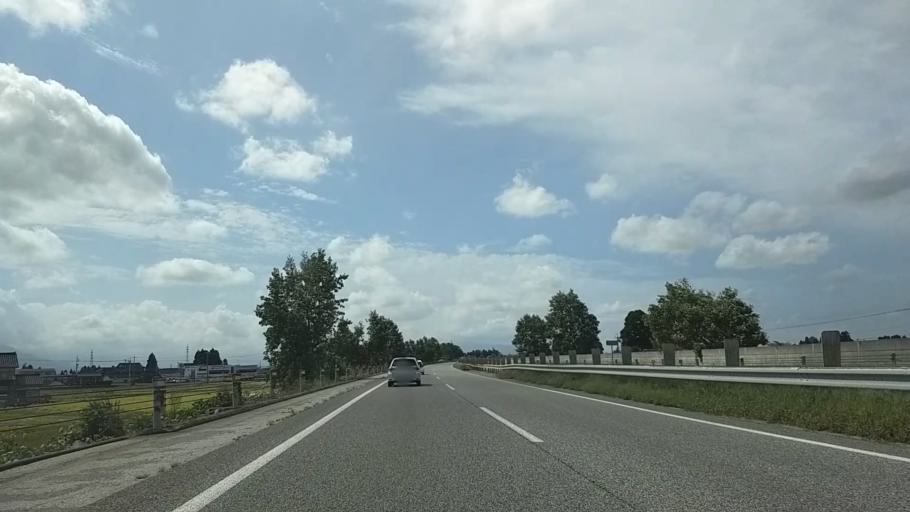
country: JP
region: Toyama
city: Takaoka
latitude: 36.6655
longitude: 137.0265
